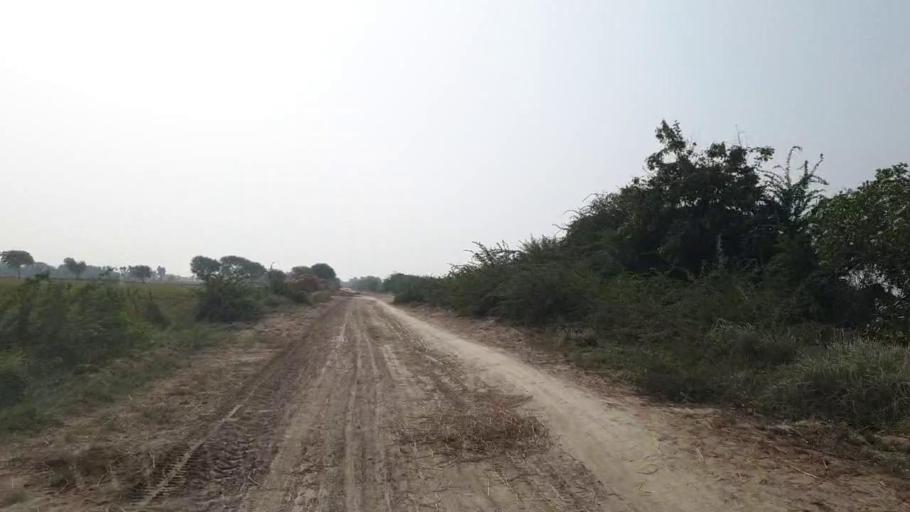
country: PK
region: Sindh
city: Kario
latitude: 24.7623
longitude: 68.5637
